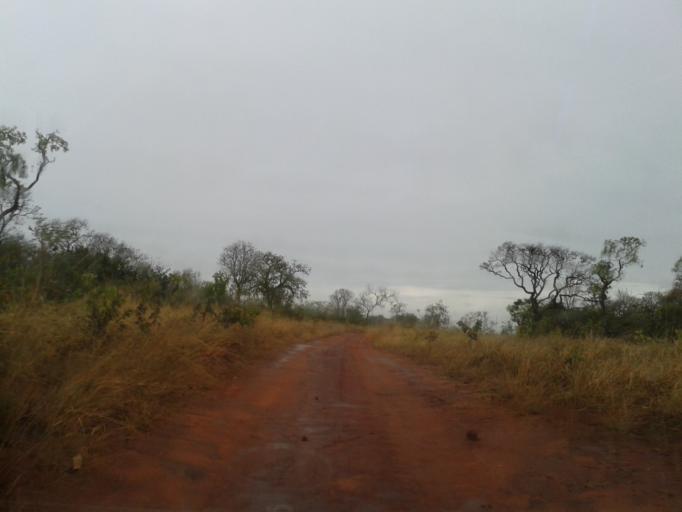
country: BR
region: Minas Gerais
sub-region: Campina Verde
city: Campina Verde
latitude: -19.3271
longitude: -49.5156
